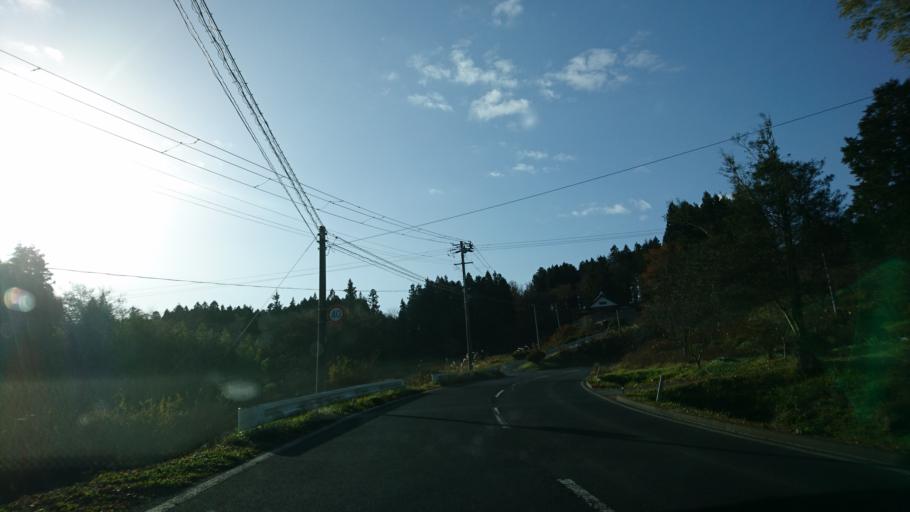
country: JP
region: Iwate
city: Ichinoseki
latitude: 38.8915
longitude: 141.2868
